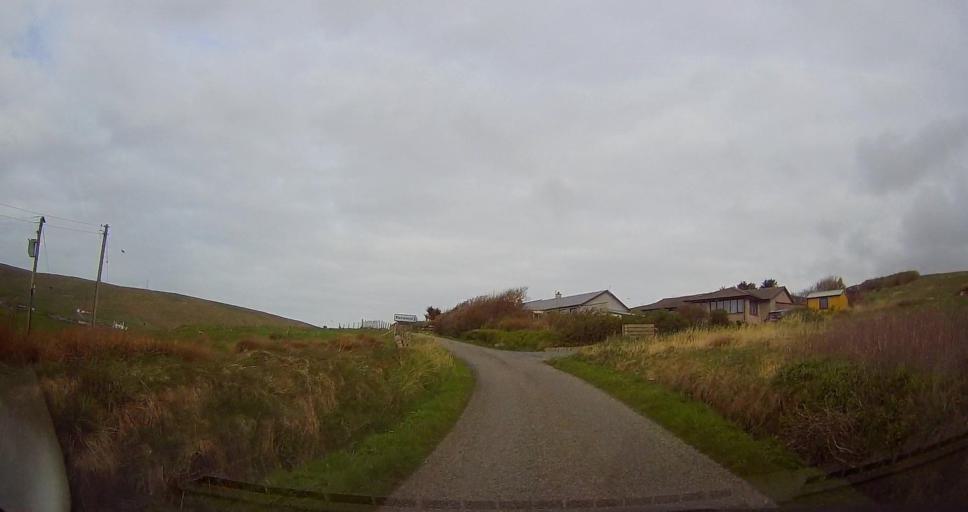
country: GB
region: Scotland
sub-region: Shetland Islands
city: Sandwick
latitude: 60.0490
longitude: -1.2167
